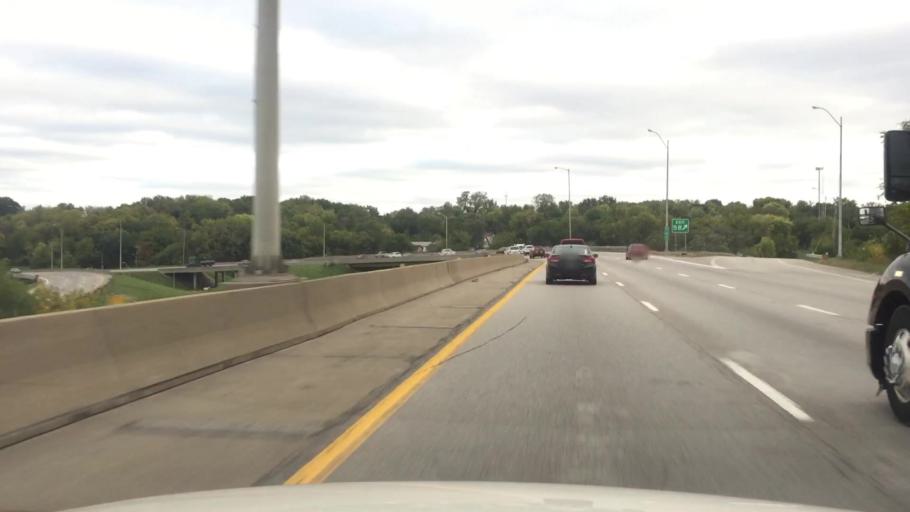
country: US
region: Missouri
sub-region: Jackson County
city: Kansas City
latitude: 39.0752
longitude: -94.5363
